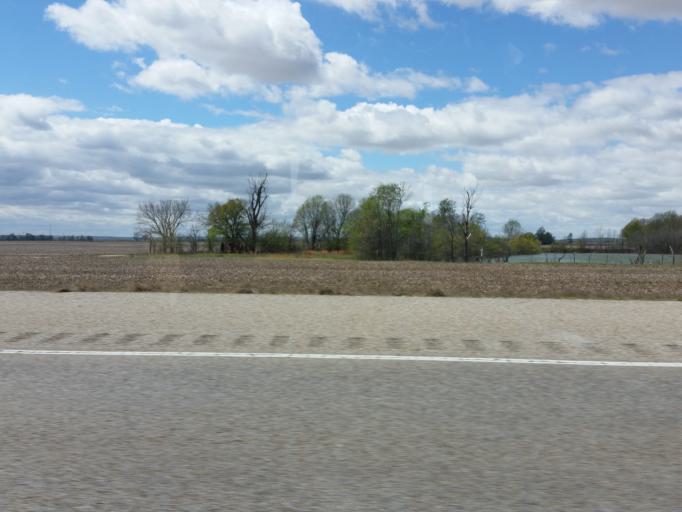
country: US
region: Arkansas
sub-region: Craighead County
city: Bay
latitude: 35.7172
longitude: -90.5796
